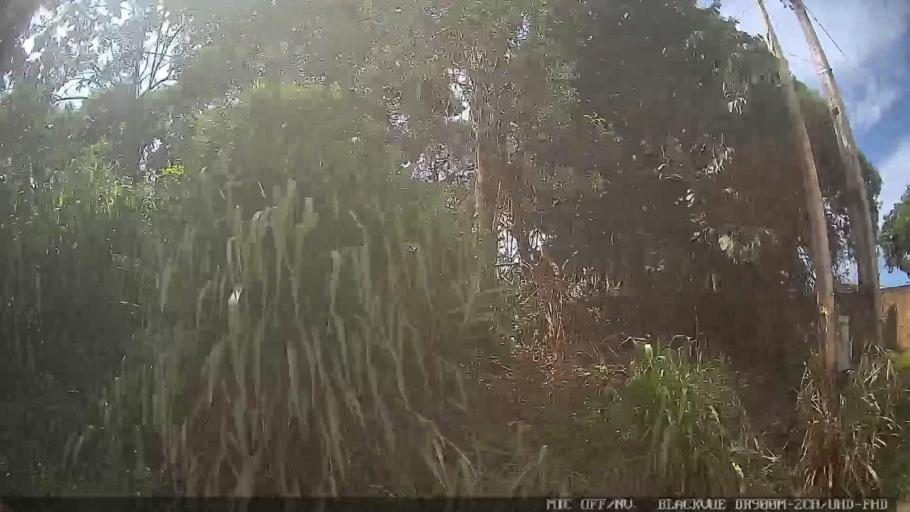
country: BR
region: Sao Paulo
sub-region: Braganca Paulista
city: Braganca Paulista
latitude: -22.9903
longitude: -46.6555
